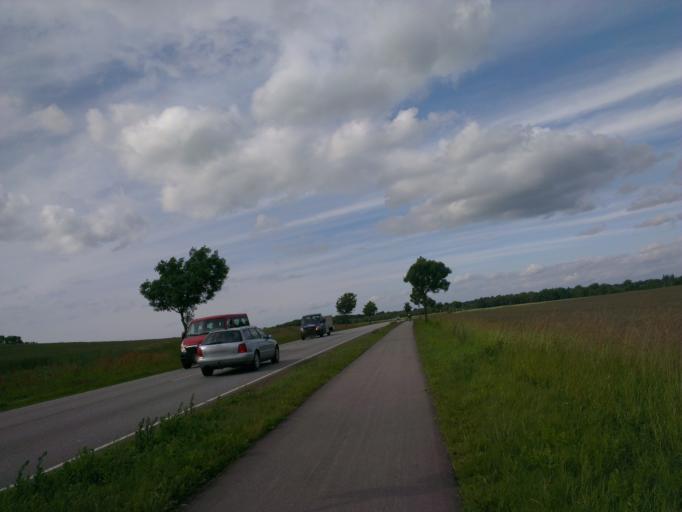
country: DK
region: Capital Region
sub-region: Frederikssund Kommune
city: Skibby
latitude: 55.7305
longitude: 11.9458
